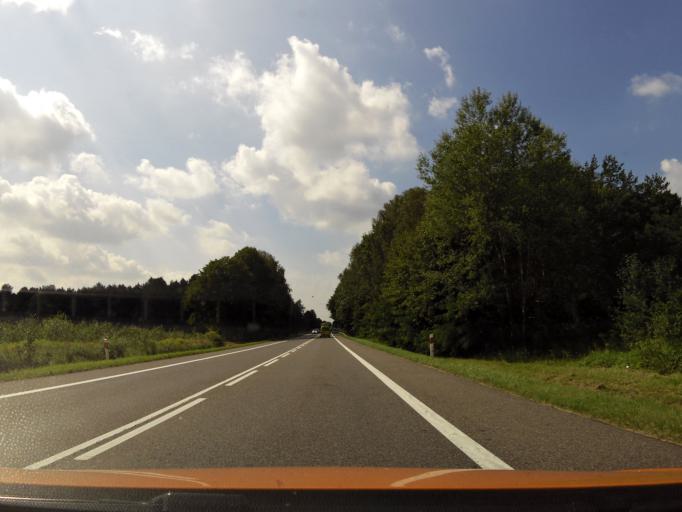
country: PL
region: West Pomeranian Voivodeship
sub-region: Powiat goleniowski
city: Goleniow
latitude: 53.5937
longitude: 14.8743
